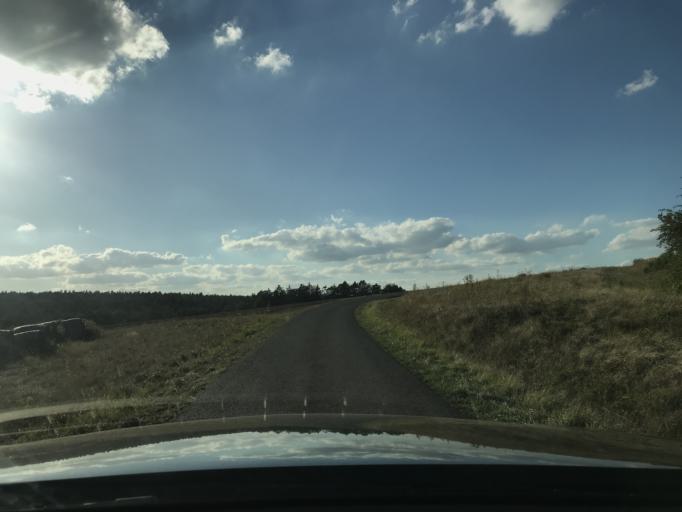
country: DE
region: Bavaria
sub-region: Regierungsbezirk Unterfranken
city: Breitbrunn
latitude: 50.0251
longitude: 10.6851
